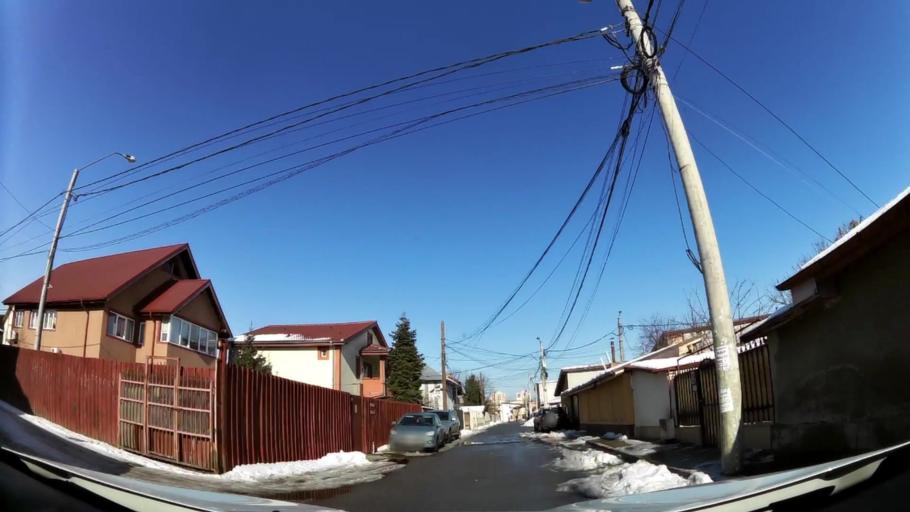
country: RO
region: Ilfov
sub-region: Comuna Magurele
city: Magurele
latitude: 44.3969
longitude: 26.0518
